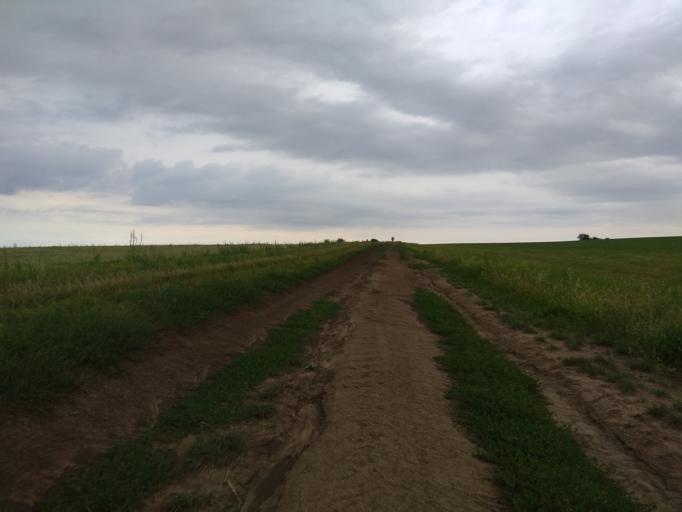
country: HU
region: Borsod-Abauj-Zemplen
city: Megyaszo
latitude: 48.1780
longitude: 21.0993
